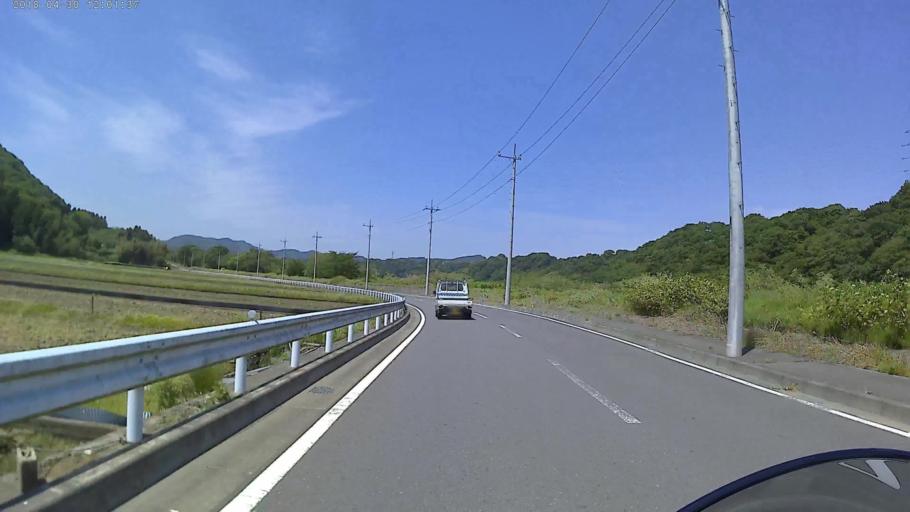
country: JP
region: Kanagawa
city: Zama
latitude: 35.5186
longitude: 139.3245
